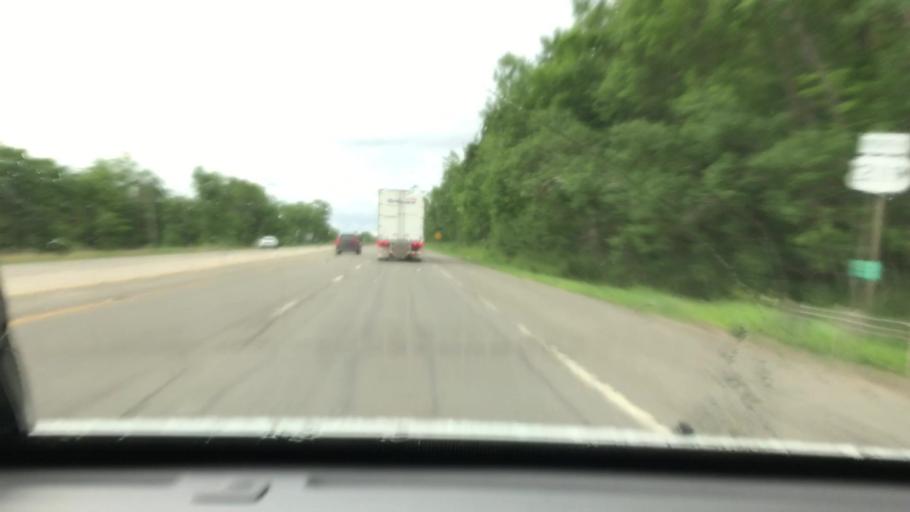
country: US
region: Pennsylvania
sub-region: McKean County
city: Foster Brook
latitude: 42.0534
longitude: -78.6356
